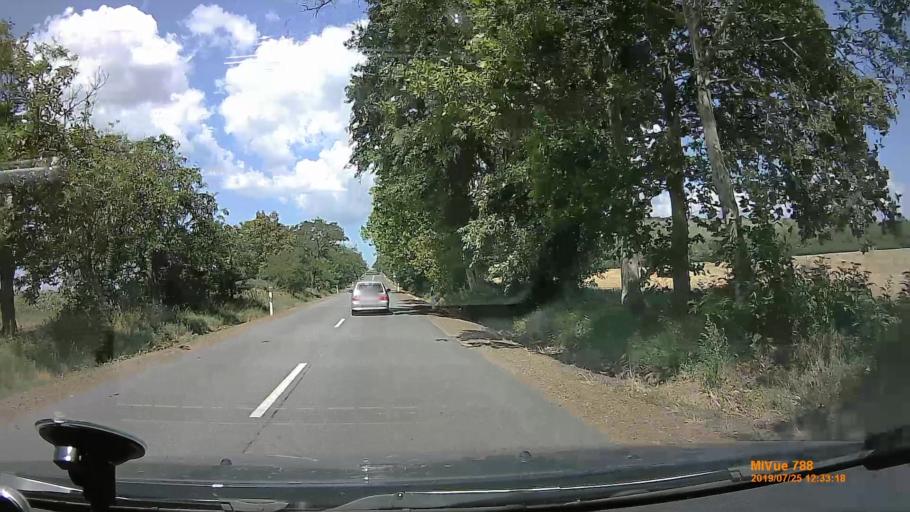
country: HU
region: Borsod-Abauj-Zemplen
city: Mad
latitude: 48.1606
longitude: 21.3084
